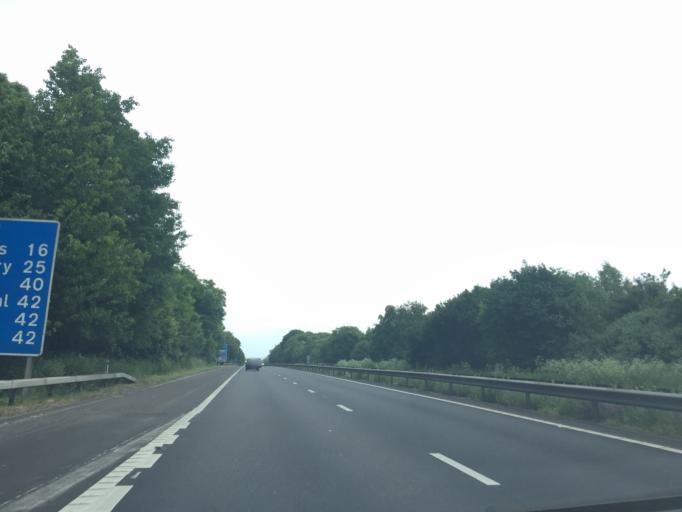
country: GB
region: England
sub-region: Kent
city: Rainham
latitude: 51.3378
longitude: 0.5913
